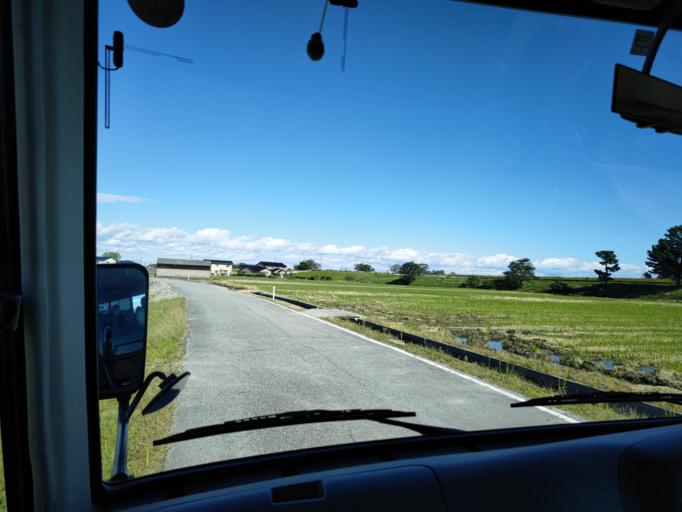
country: JP
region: Toyama
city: Nyuzen
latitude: 36.9094
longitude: 137.4347
